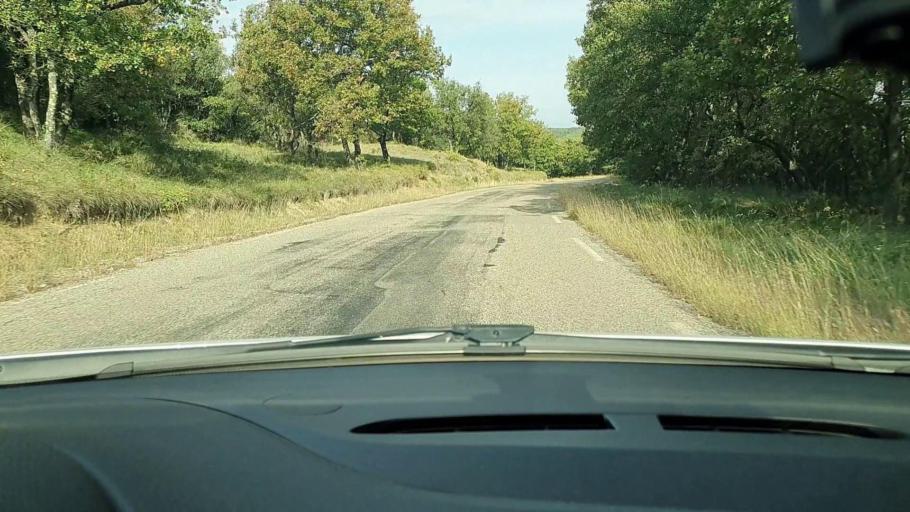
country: FR
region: Languedoc-Roussillon
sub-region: Departement du Gard
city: Saint-Quentin-la-Poterie
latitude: 44.1283
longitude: 4.4037
